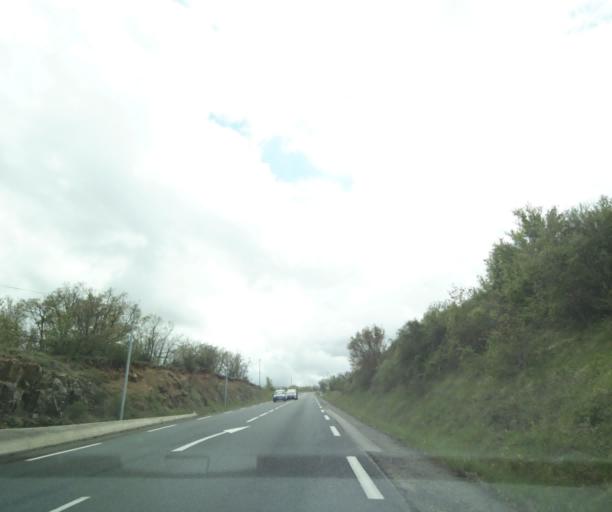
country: FR
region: Midi-Pyrenees
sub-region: Departement de l'Aveyron
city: Millau
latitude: 44.0832
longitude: 3.1251
